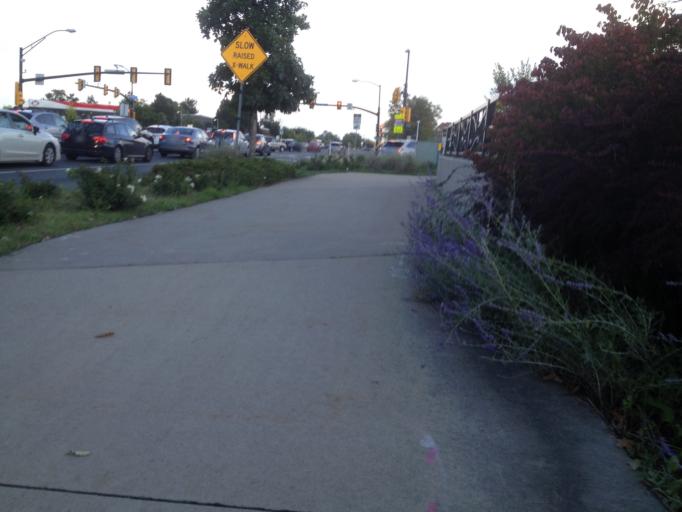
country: US
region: Colorado
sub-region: Boulder County
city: Boulder
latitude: 39.9860
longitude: -105.2505
